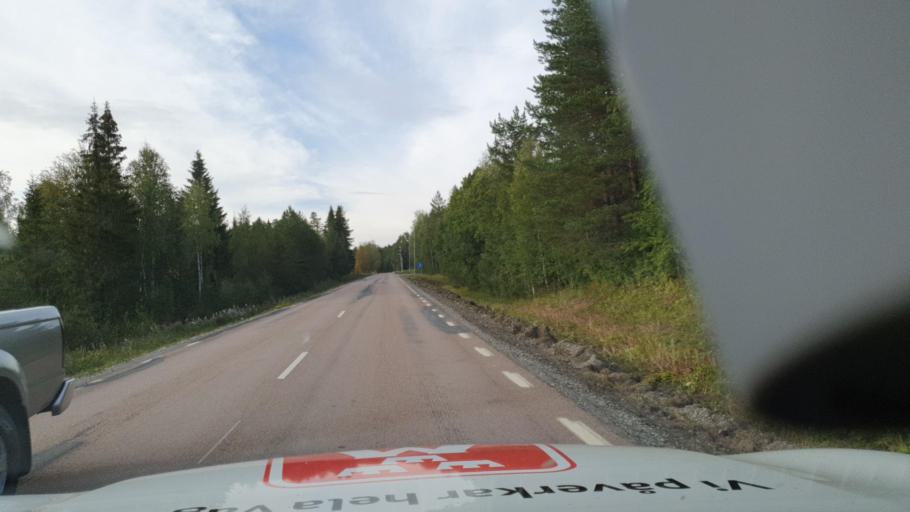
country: SE
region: Jaemtland
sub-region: Stroemsunds Kommun
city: Stroemsund
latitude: 63.7967
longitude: 15.7051
